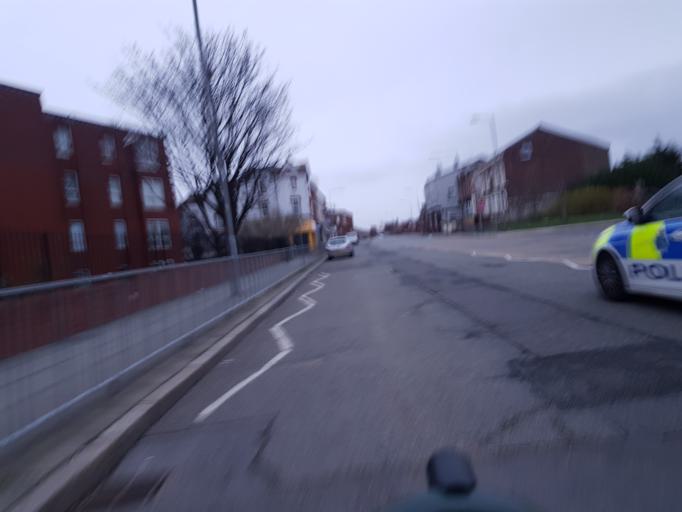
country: GB
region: England
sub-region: Liverpool
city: Liverpool
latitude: 53.4259
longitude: -2.9653
